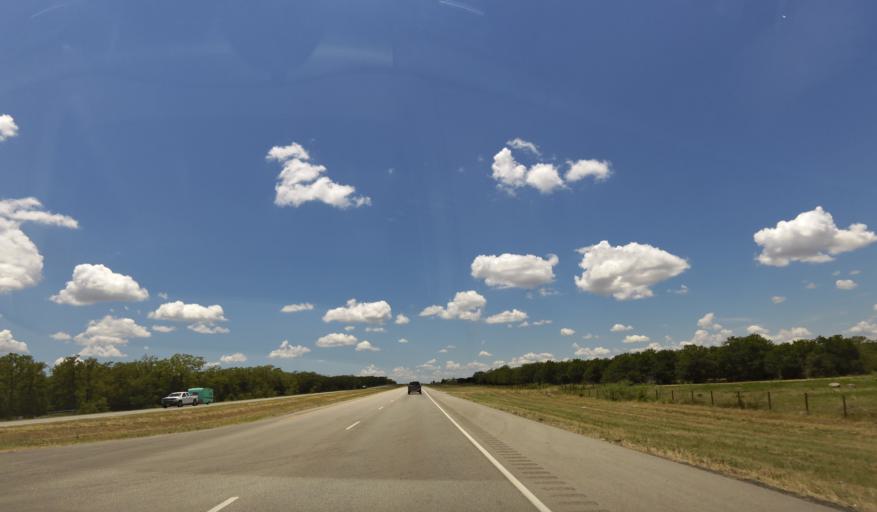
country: US
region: Texas
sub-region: Lee County
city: Giddings
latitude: 30.1436
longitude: -96.7391
